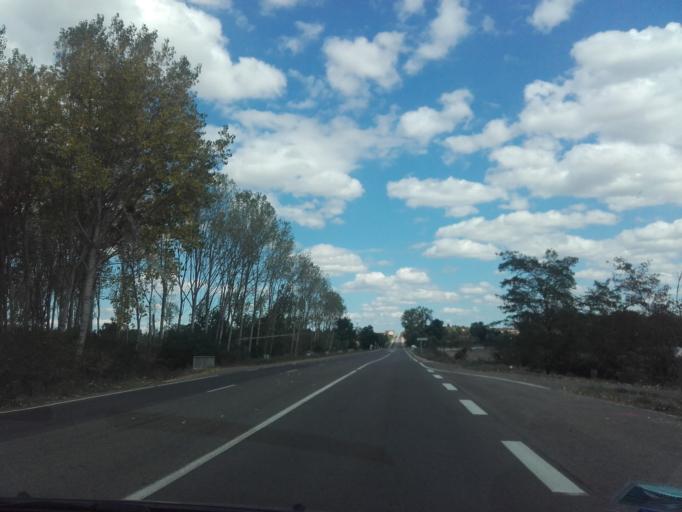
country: FR
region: Bourgogne
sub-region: Departement de Saone-et-Loire
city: La Chapelle-de-Guinchay
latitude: 46.1950
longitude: 4.7615
